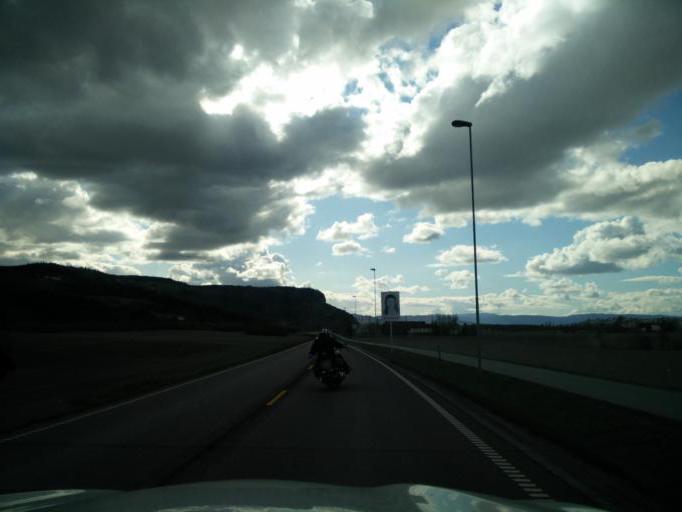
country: NO
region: Sor-Trondelag
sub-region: Melhus
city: Melhus
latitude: 63.3247
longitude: 10.2880
